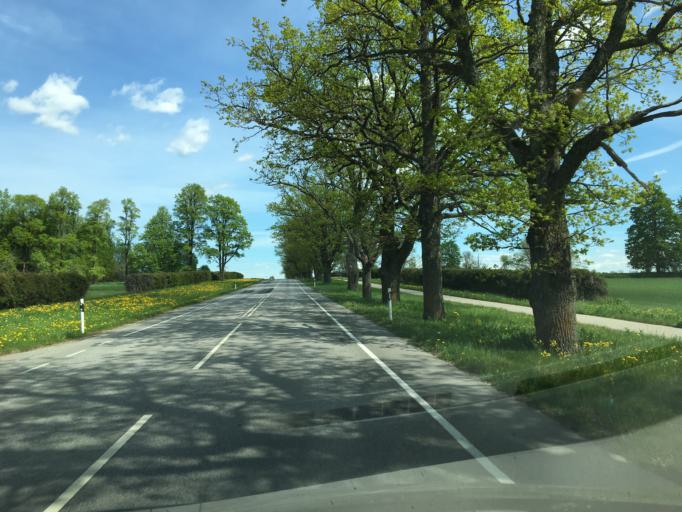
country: EE
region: Vorumaa
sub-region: Antsla vald
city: Vana-Antsla
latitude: 57.9140
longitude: 26.3035
